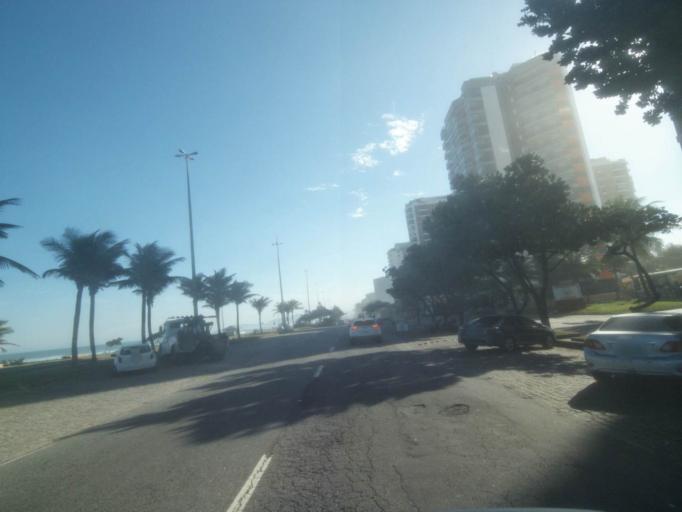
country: BR
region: Rio de Janeiro
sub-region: Rio De Janeiro
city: Rio de Janeiro
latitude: -23.0103
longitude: -43.3561
